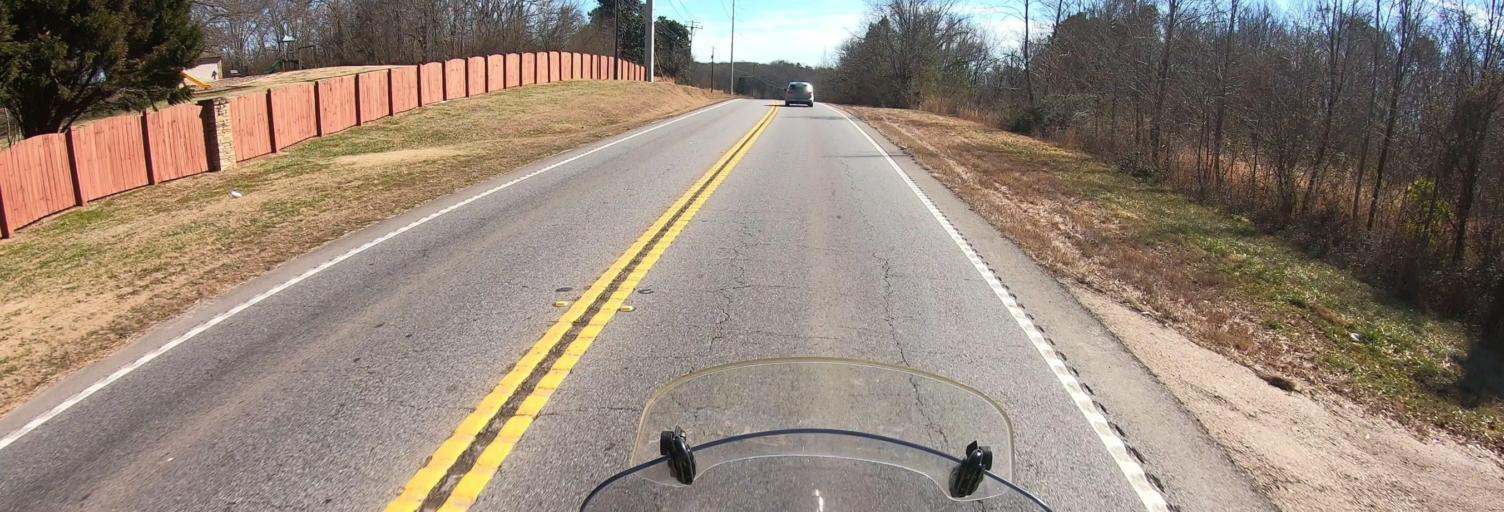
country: US
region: Georgia
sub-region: Forsyth County
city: Cumming
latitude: 34.2782
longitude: -84.1197
